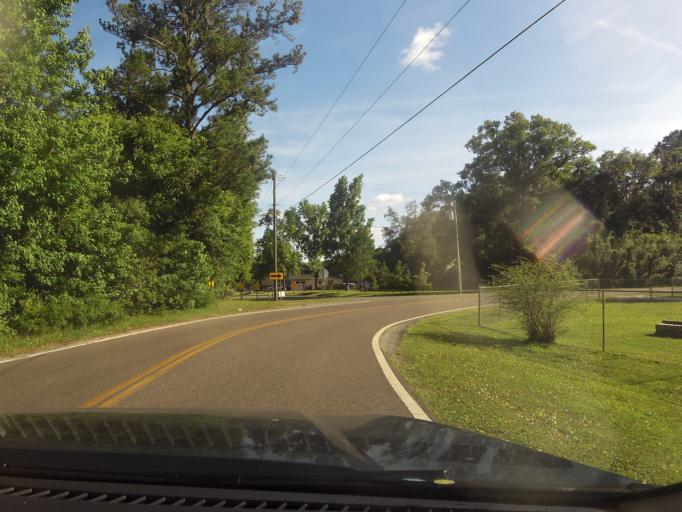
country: US
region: Florida
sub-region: Nassau County
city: Nassau Village-Ratliff
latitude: 30.5108
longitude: -81.7819
